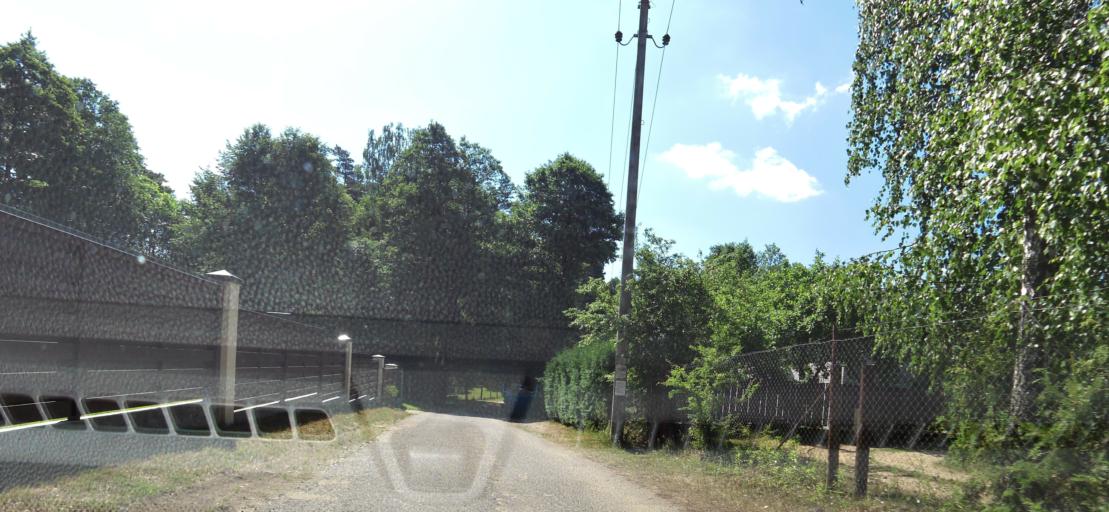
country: LT
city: Nemencine
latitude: 54.7985
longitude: 25.3996
